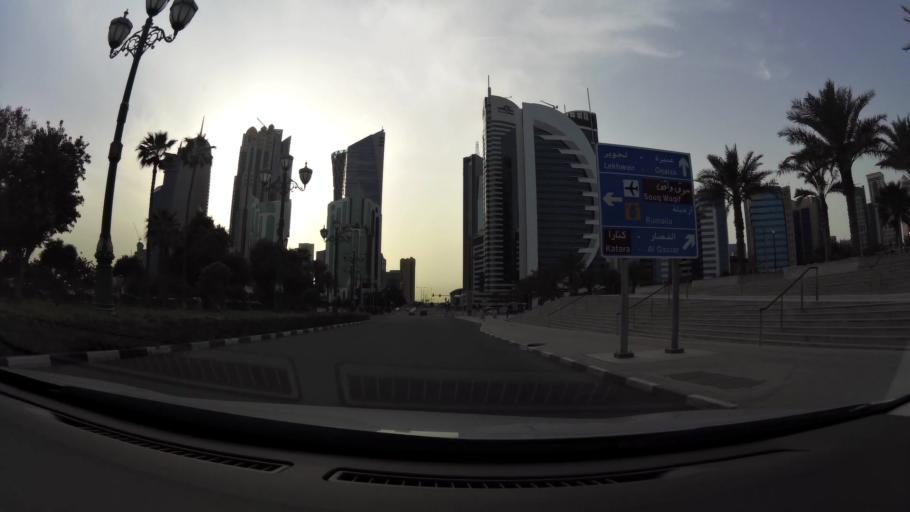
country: QA
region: Baladiyat ad Dawhah
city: Doha
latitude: 25.3187
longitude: 51.5337
